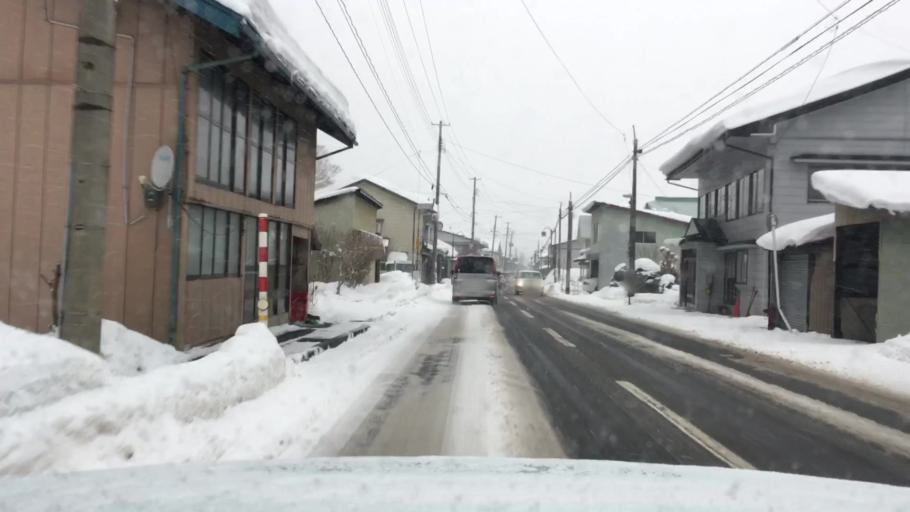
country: JP
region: Iwate
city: Ichinohe
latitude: 40.0949
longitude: 141.0471
